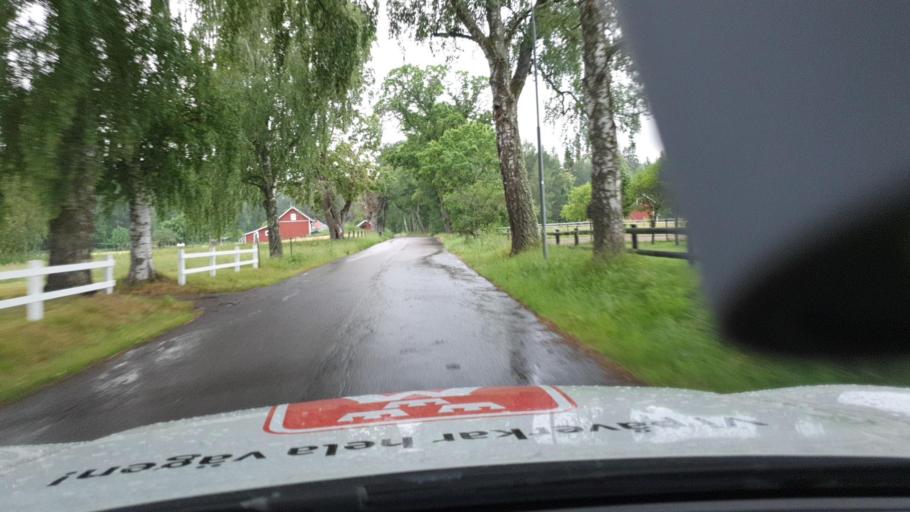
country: SE
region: Vaestra Goetaland
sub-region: Skovde Kommun
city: Stopen
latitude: 58.4257
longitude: 13.9161
